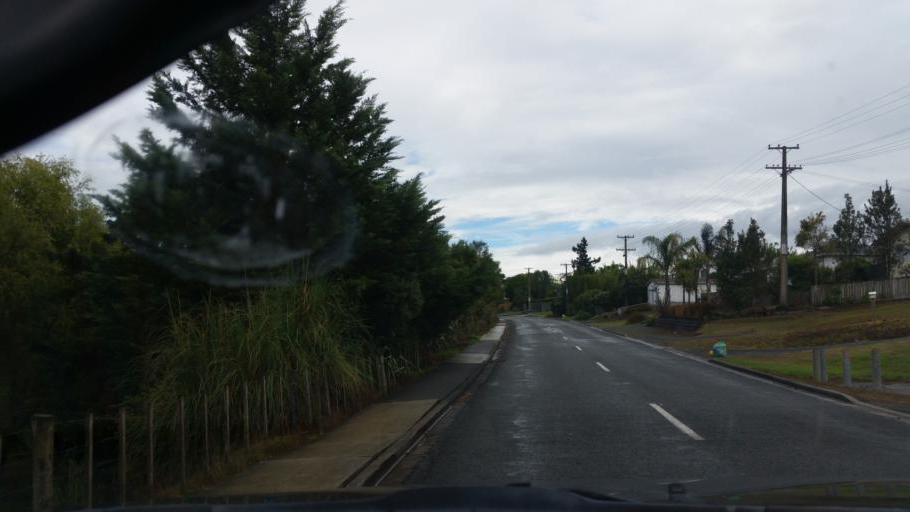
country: NZ
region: Northland
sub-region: Whangarei
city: Ruakaka
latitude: -36.1094
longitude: 174.3622
